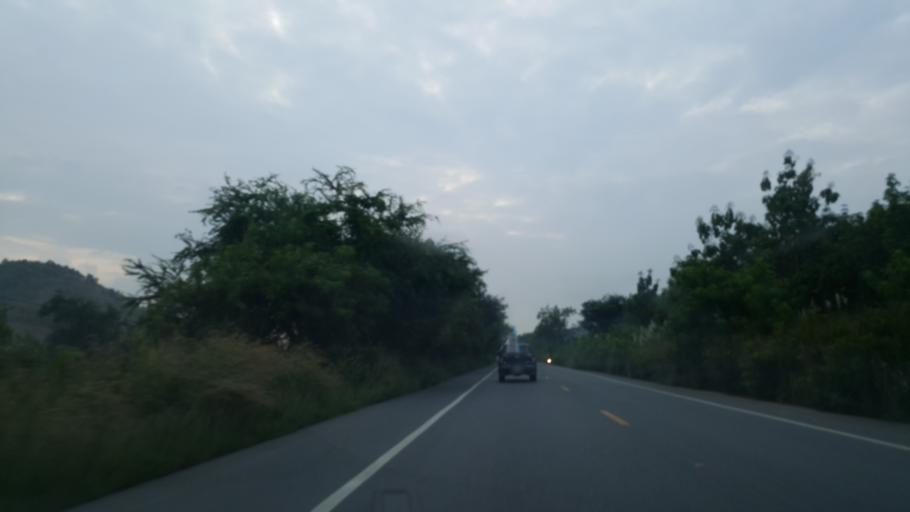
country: TH
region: Chon Buri
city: Sattahip
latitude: 12.7286
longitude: 100.9579
